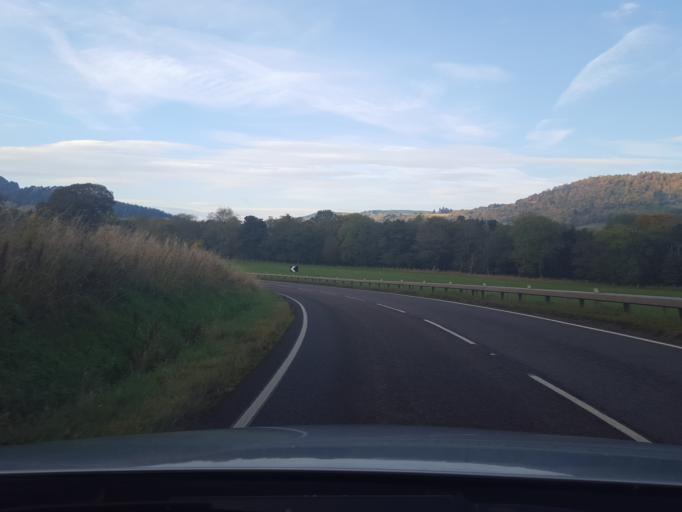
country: GB
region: Scotland
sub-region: Highland
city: Beauly
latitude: 57.3292
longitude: -4.4619
